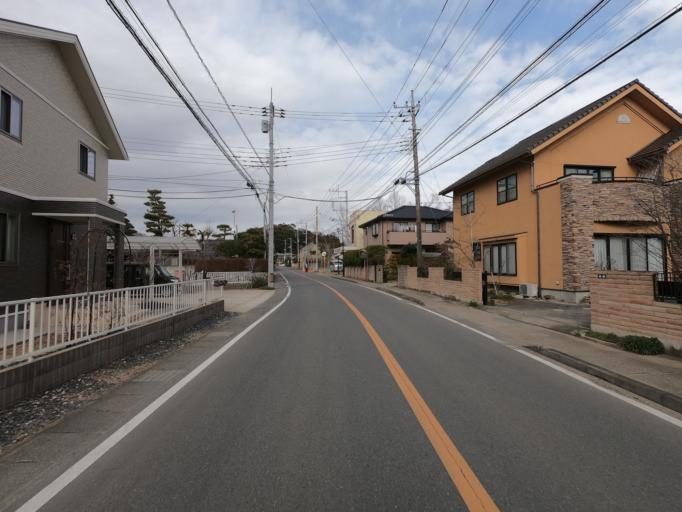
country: JP
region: Ibaraki
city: Inashiki
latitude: 36.0903
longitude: 140.4250
